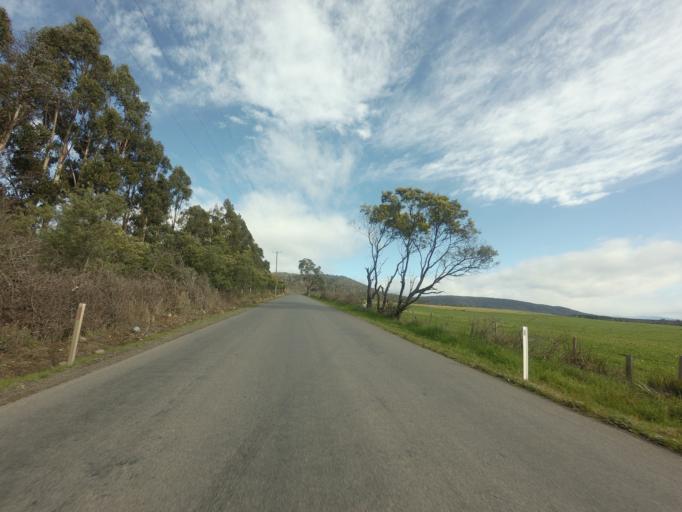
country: AU
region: Tasmania
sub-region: Derwent Valley
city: New Norfolk
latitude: -42.7822
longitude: 147.0008
